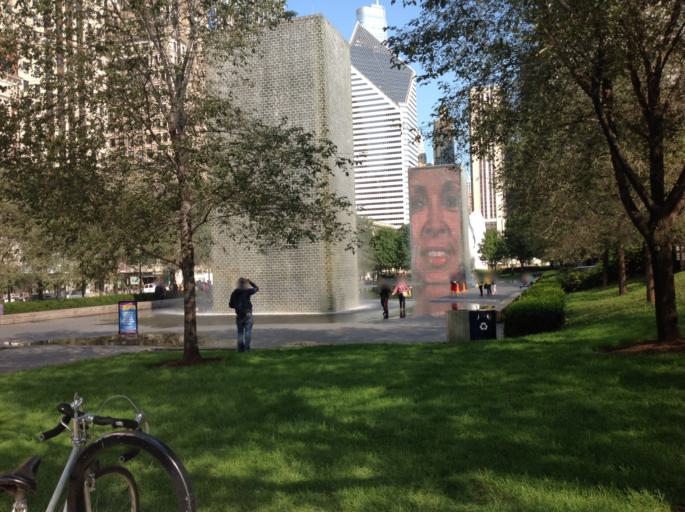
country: US
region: Illinois
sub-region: Cook County
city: Chicago
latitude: 41.8810
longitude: -87.6236
